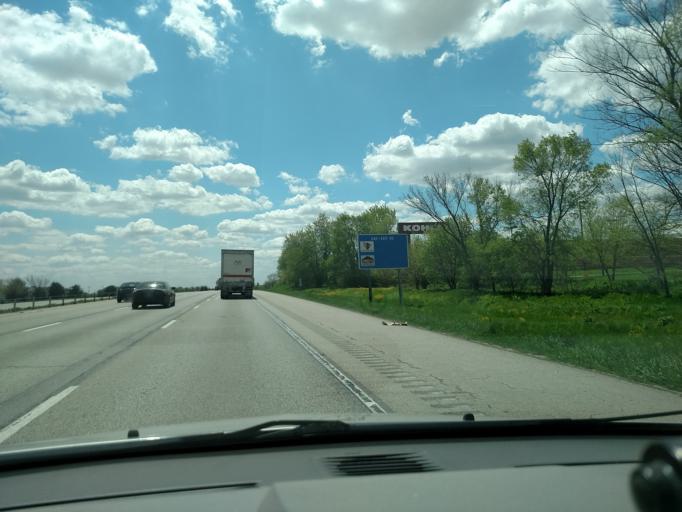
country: US
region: Iowa
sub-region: Polk County
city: Ankeny
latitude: 41.7114
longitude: -93.5765
